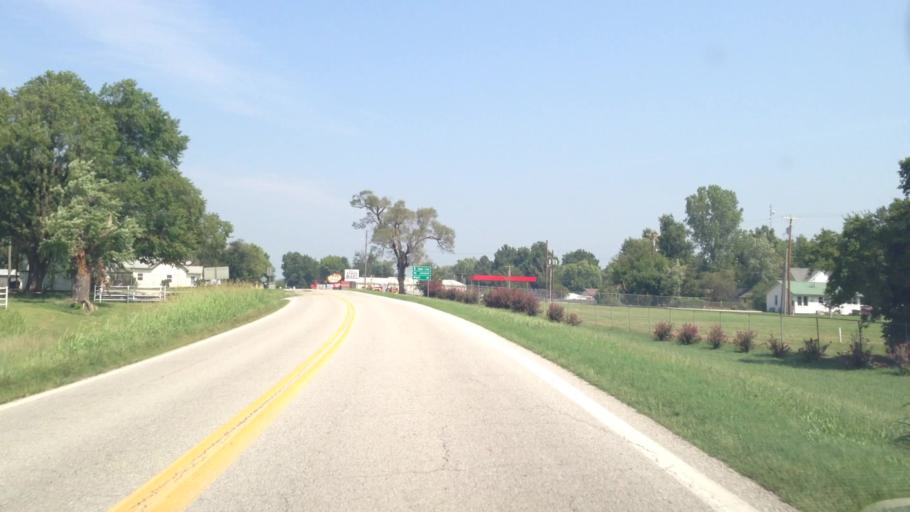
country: US
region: Kansas
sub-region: Labette County
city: Chetopa
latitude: 36.8712
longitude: -95.0989
